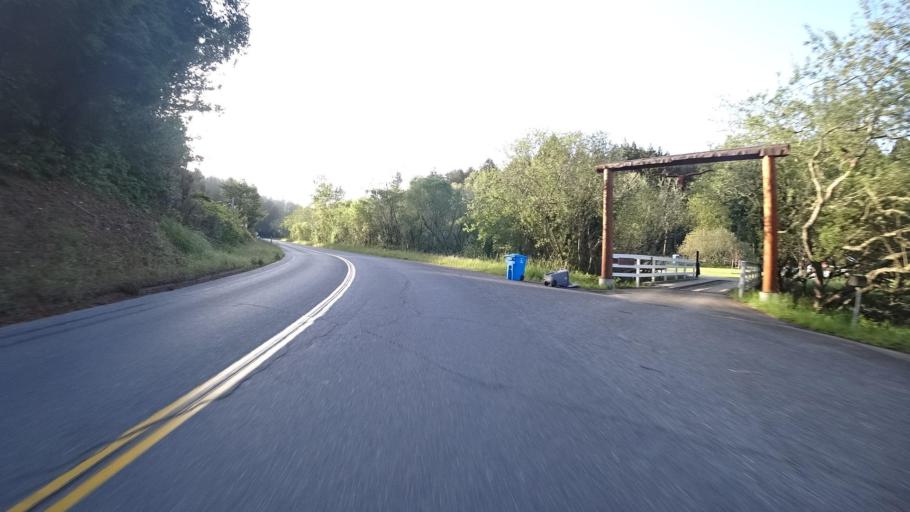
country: US
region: California
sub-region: Humboldt County
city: Myrtletown
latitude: 40.7778
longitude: -124.1184
